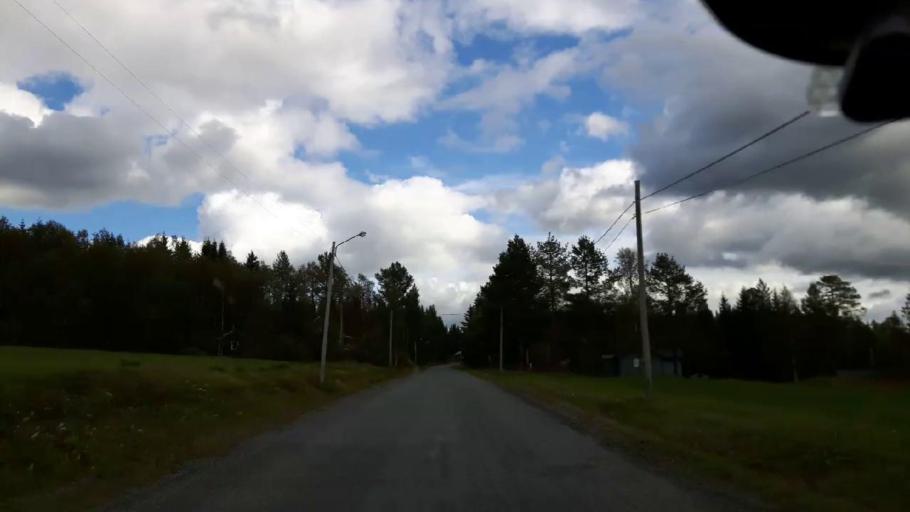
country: SE
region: Jaemtland
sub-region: Stroemsunds Kommun
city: Stroemsund
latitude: 63.4209
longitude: 15.8336
